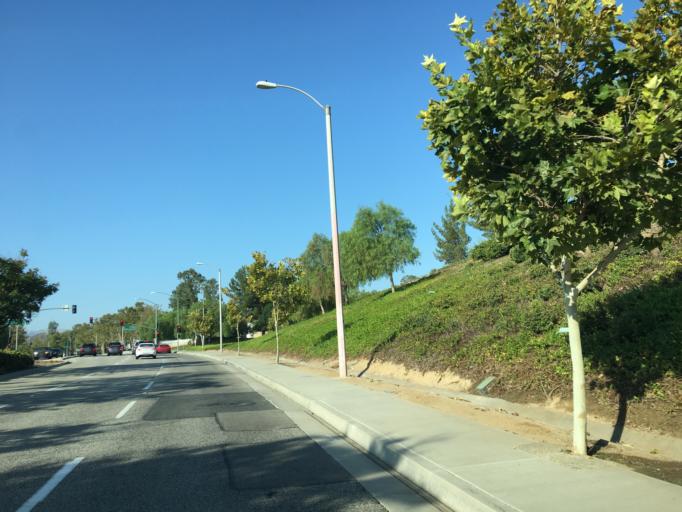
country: US
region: California
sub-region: Los Angeles County
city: Valencia
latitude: 34.4520
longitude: -118.6250
